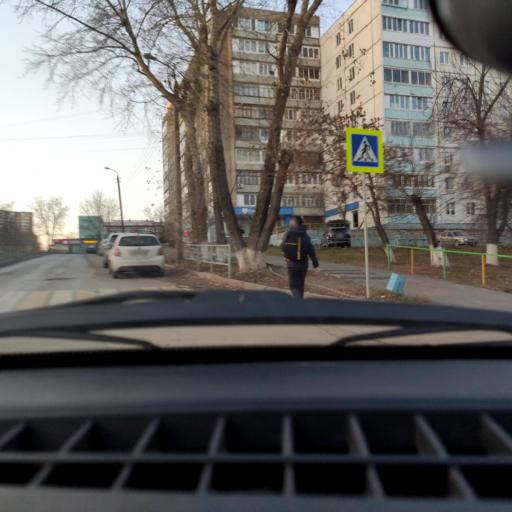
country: RU
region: Bashkortostan
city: Ufa
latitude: 54.7345
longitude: 55.9944
